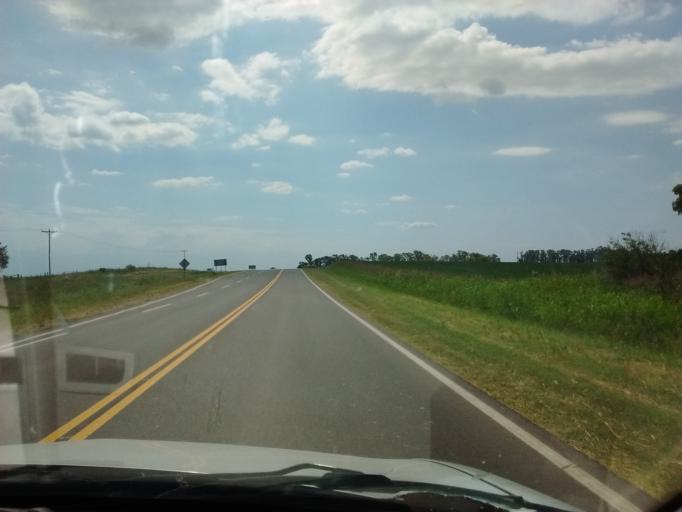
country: AR
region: Entre Rios
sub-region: Departamento de Victoria
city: Victoria
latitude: -32.6583
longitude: -60.0581
